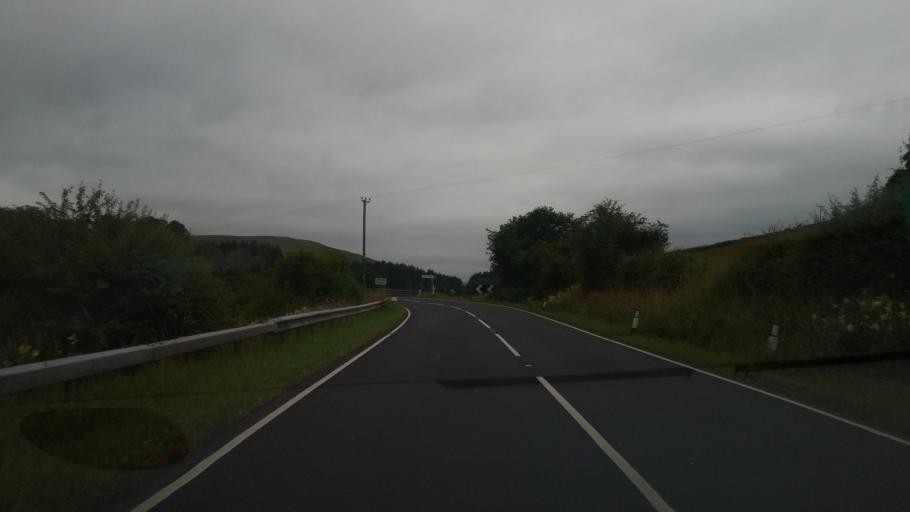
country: GB
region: Scotland
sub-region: The Scottish Borders
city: Hawick
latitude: 55.3641
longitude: -2.8901
